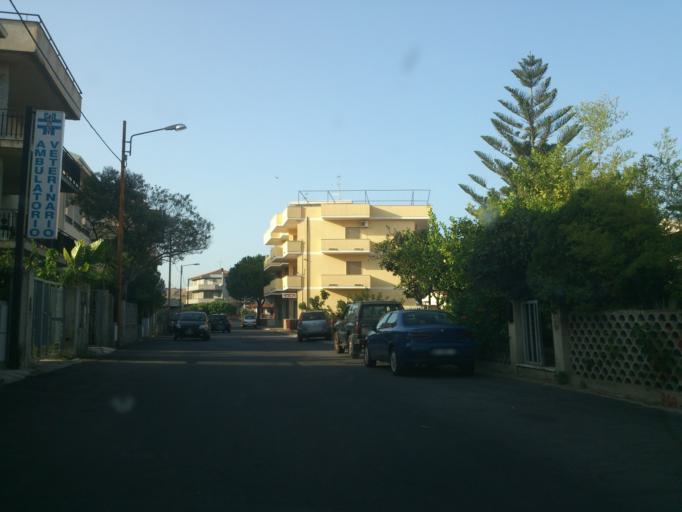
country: IT
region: Calabria
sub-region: Provincia di Reggio Calabria
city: Monasterace Marina
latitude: 38.4374
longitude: 16.5721
